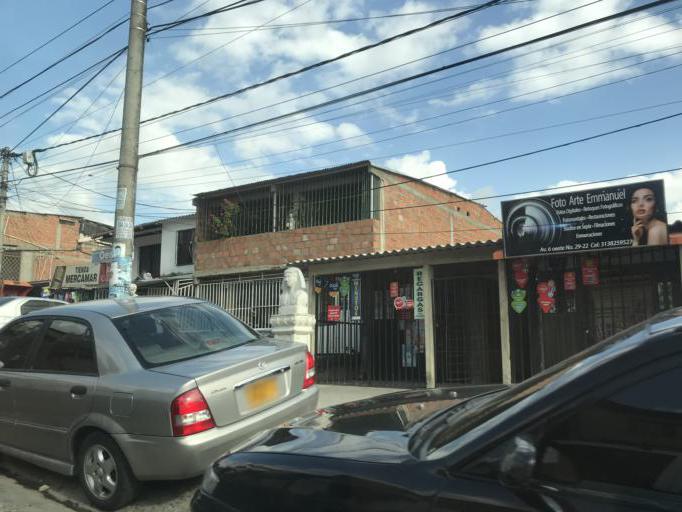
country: CO
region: Valle del Cauca
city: Cali
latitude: 3.4542
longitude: -76.5748
